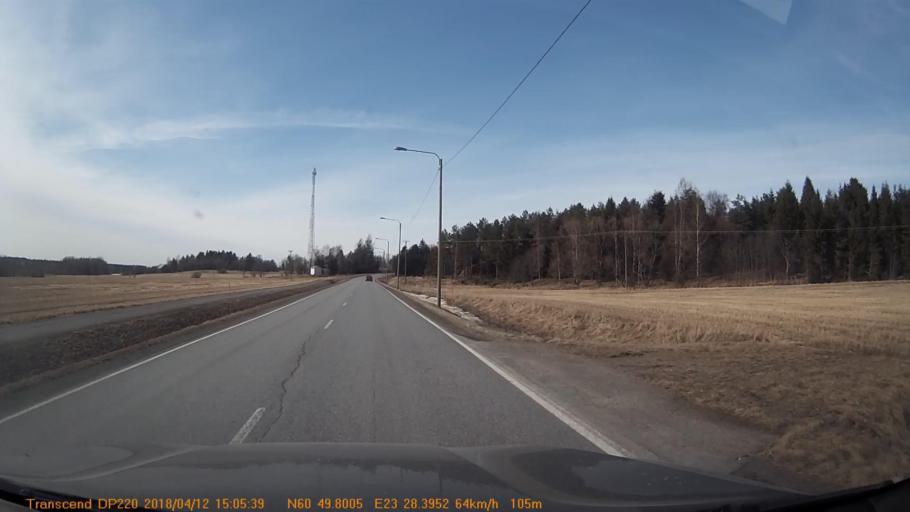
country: FI
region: Haeme
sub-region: Forssa
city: Jokioinen
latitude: 60.8303
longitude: 23.4728
